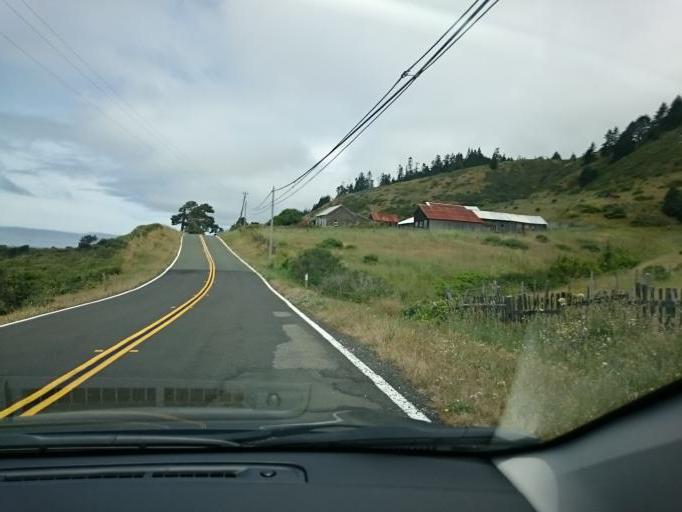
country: US
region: California
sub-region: Mendocino County
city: Fort Bragg
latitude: 39.1690
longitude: -123.7433
